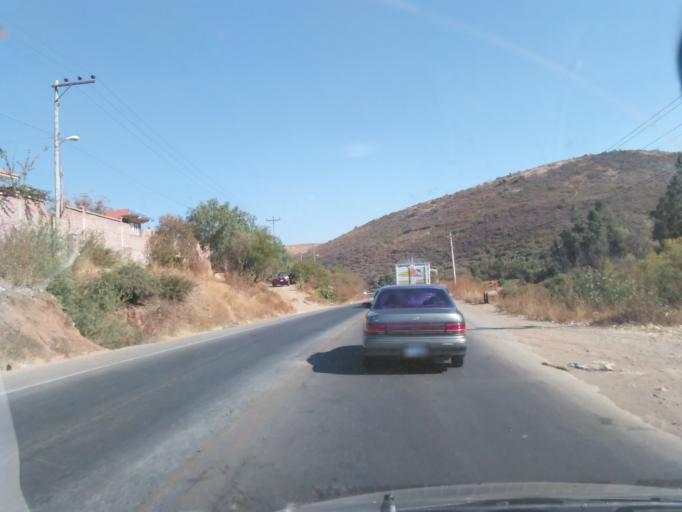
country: BO
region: Cochabamba
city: Tarata
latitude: -17.5087
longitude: -66.0890
